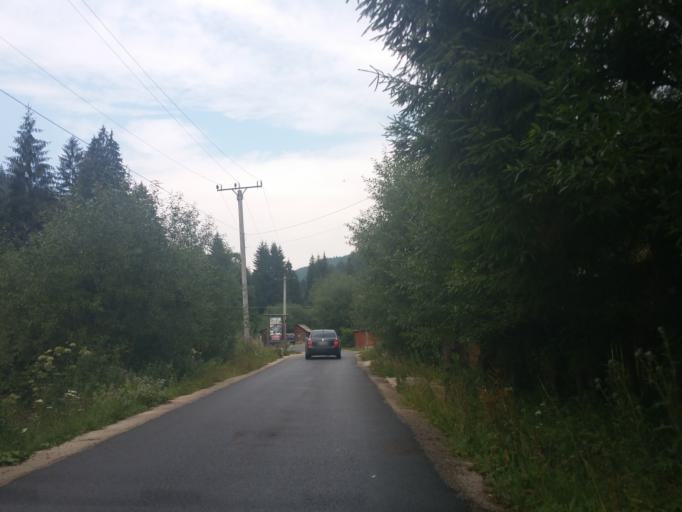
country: RO
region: Alba
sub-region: Comuna Garda de Sus
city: Garda de Sus
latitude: 46.4672
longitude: 22.8213
